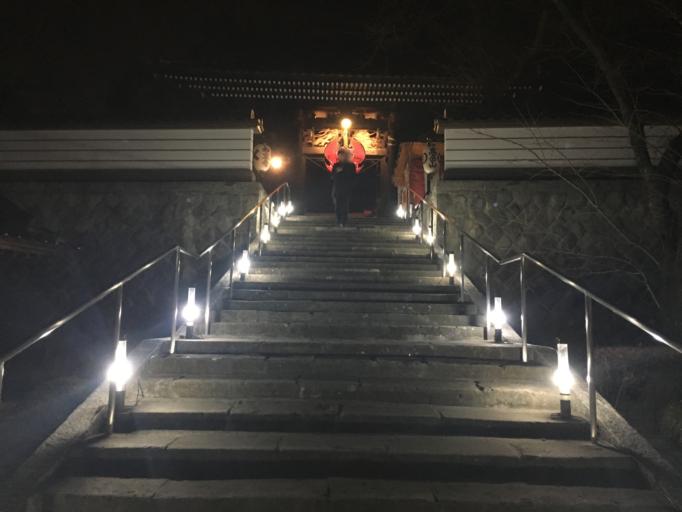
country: JP
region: Fukushima
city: Koriyama
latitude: 37.3952
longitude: 140.3791
